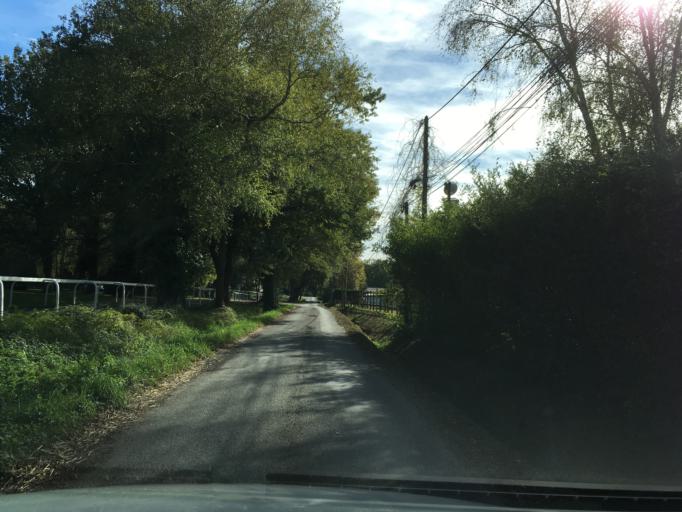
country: FR
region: Aquitaine
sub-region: Departement des Pyrenees-Atlantiques
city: Montardon
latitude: 43.3423
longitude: -0.3696
